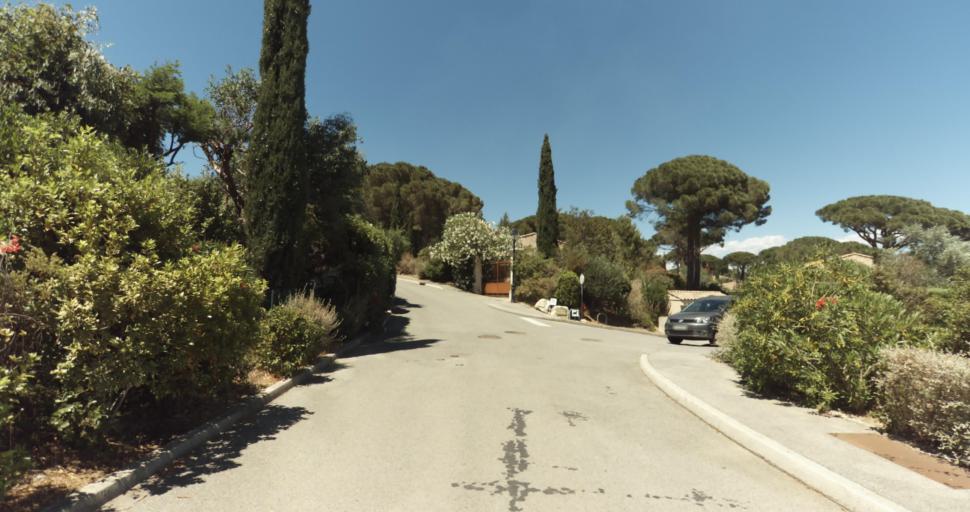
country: FR
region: Provence-Alpes-Cote d'Azur
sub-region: Departement du Var
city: Gassin
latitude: 43.2532
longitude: 6.5713
